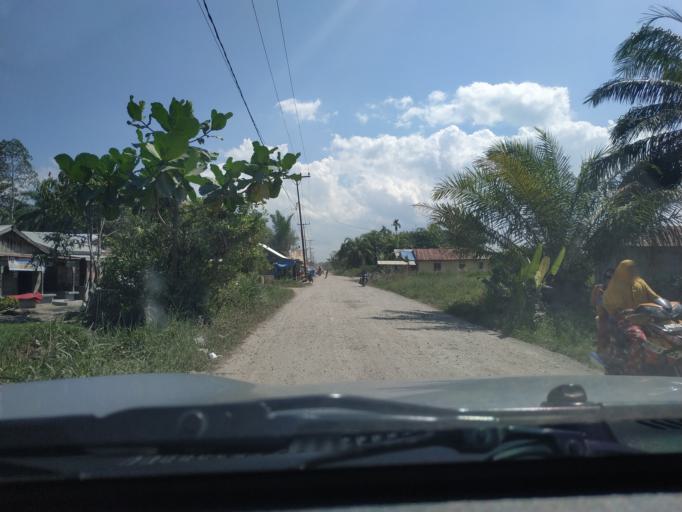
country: ID
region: North Sumatra
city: Tanjungbalai
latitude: 2.8866
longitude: 99.8616
